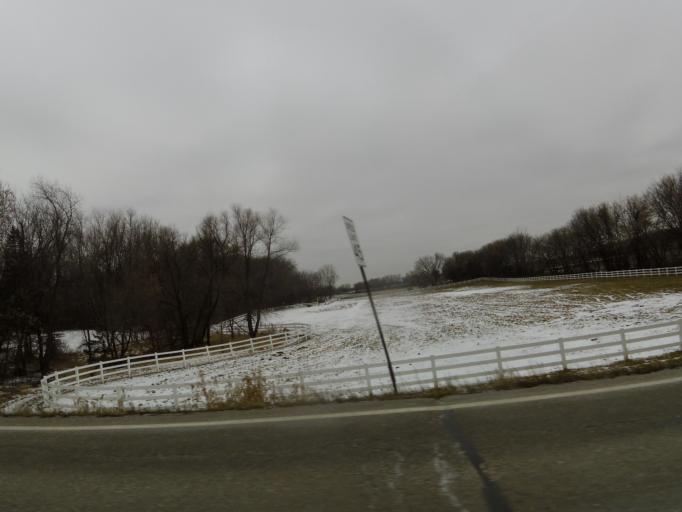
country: US
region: Minnesota
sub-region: Hennepin County
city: Independence
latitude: 44.9919
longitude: -93.7272
